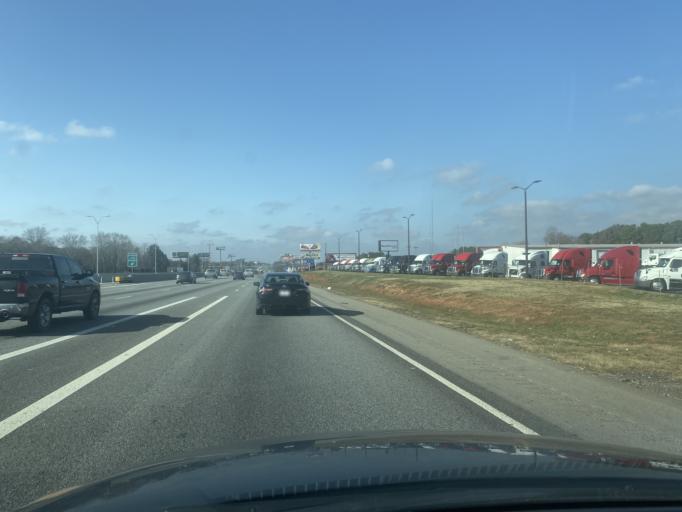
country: US
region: Georgia
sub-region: Henry County
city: McDonough
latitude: 33.4153
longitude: -84.1658
